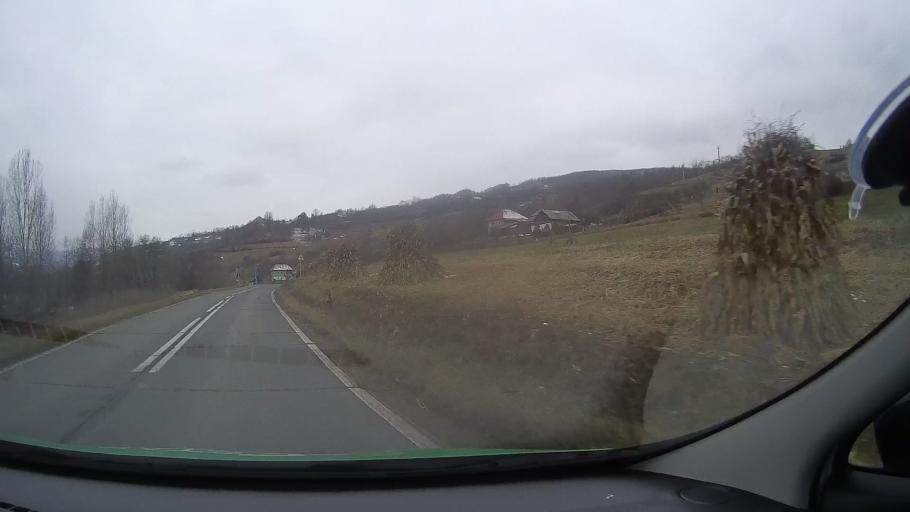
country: RO
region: Alba
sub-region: Comuna Metes
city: Metes
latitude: 46.1045
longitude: 23.4385
